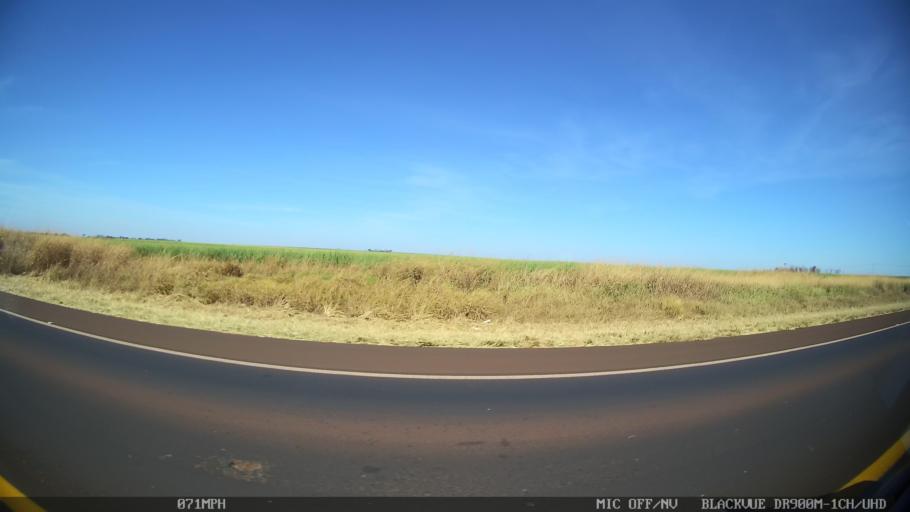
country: BR
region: Sao Paulo
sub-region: Barretos
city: Barretos
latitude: -20.4797
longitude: -48.5017
